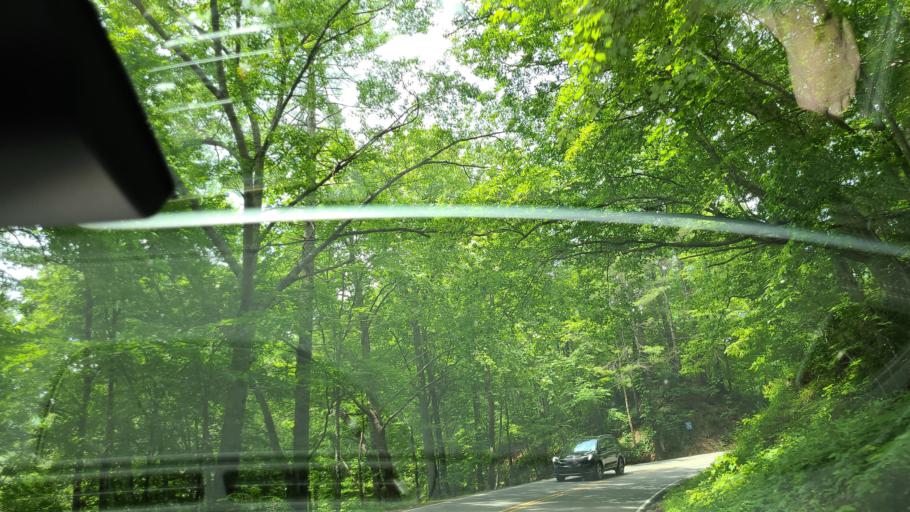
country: US
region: North Carolina
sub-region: Macon County
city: Franklin
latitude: 35.1260
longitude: -83.2811
